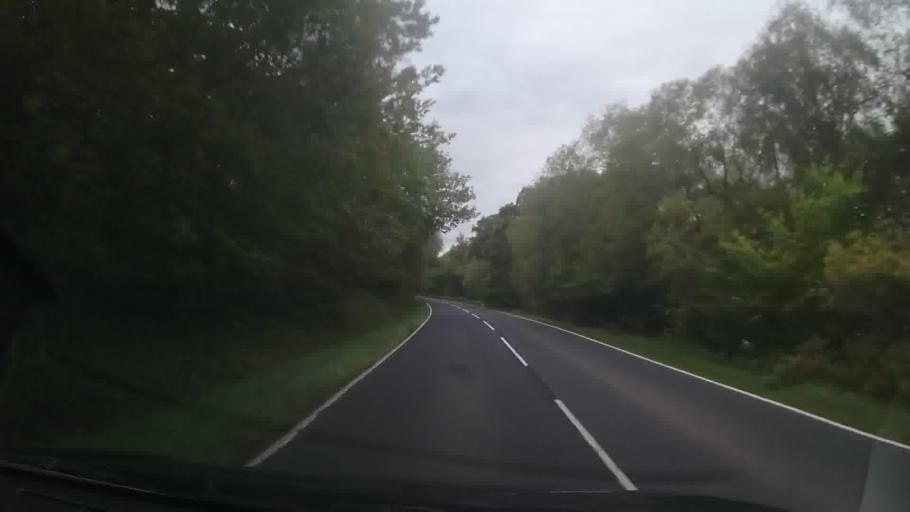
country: GB
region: Scotland
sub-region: Argyll and Bute
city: Garelochhead
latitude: 56.2098
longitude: -5.0563
